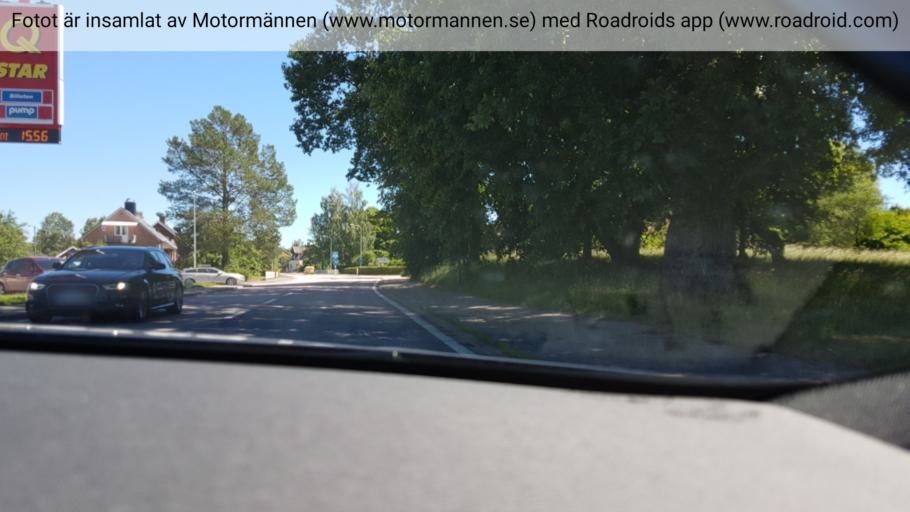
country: SE
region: Vaestra Goetaland
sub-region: Ulricehamns Kommun
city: Ulricehamn
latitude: 57.8970
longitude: 13.4570
